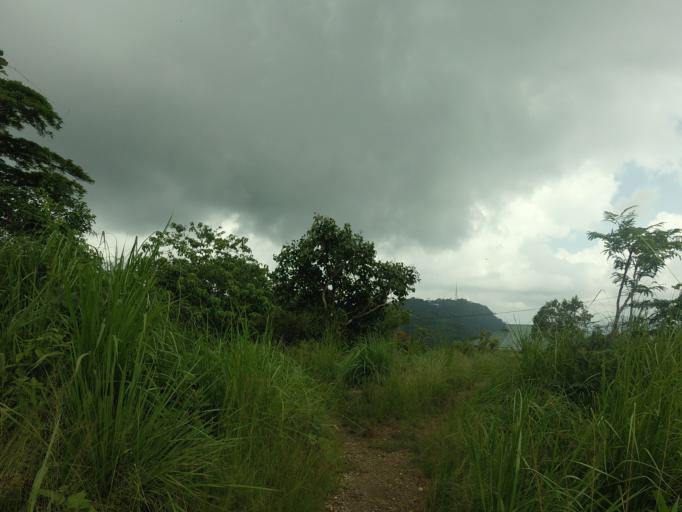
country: GH
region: Volta
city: Kpandu
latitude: 6.8529
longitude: 0.4335
